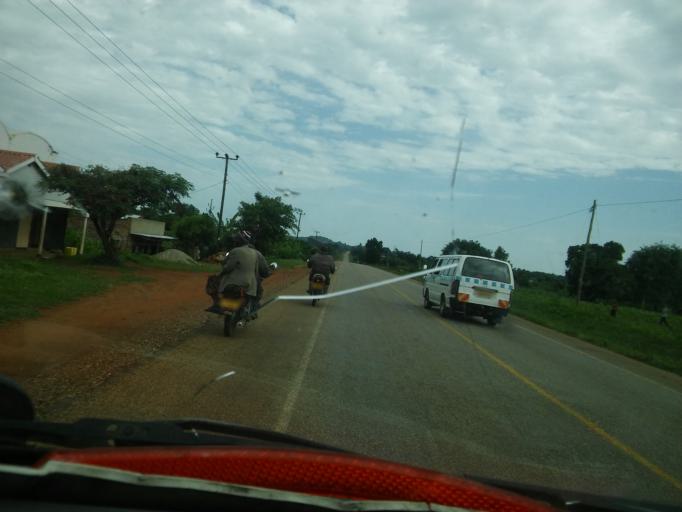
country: UG
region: Eastern Region
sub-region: Mbale District
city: Mbale
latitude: 1.1762
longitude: 34.1502
